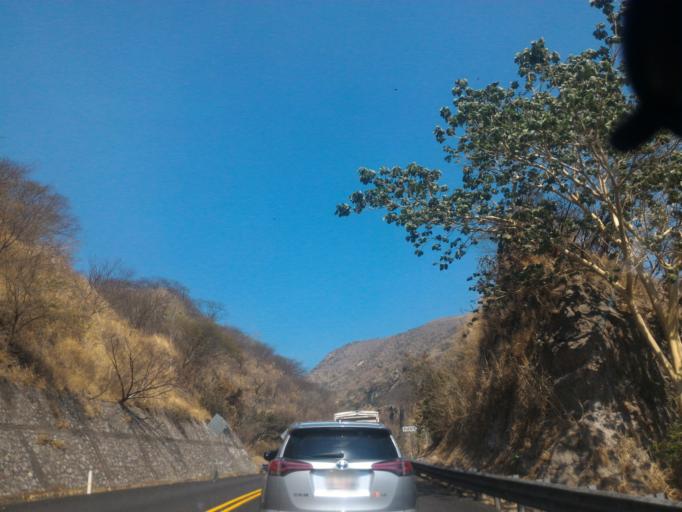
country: MX
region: Jalisco
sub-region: Tonila
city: San Marcos
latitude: 19.4965
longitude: -103.4443
